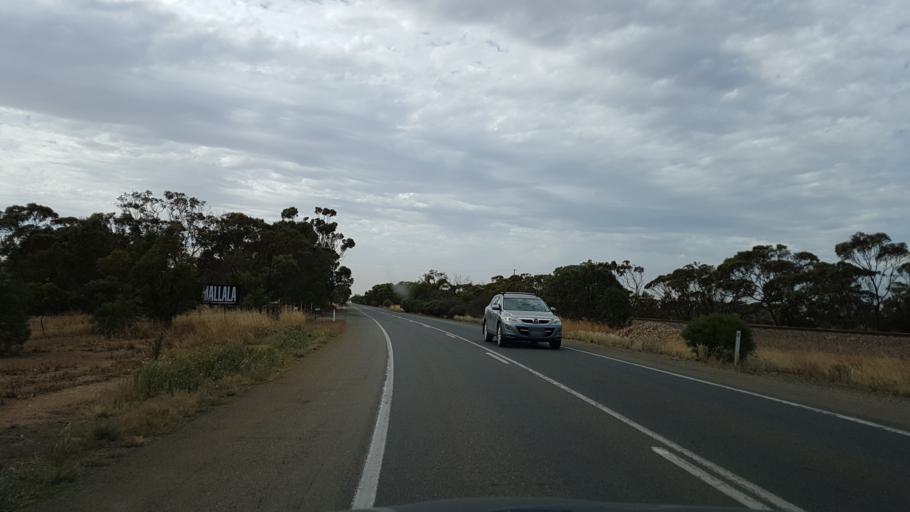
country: AU
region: South Australia
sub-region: Mallala
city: Mallala
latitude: -34.4301
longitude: 138.4936
